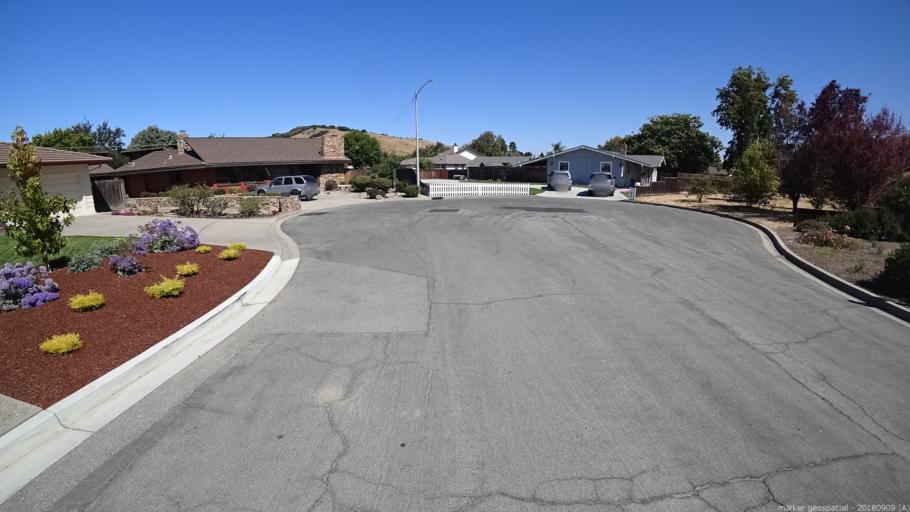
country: US
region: California
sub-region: Monterey County
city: Salinas
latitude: 36.6111
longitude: -121.6927
